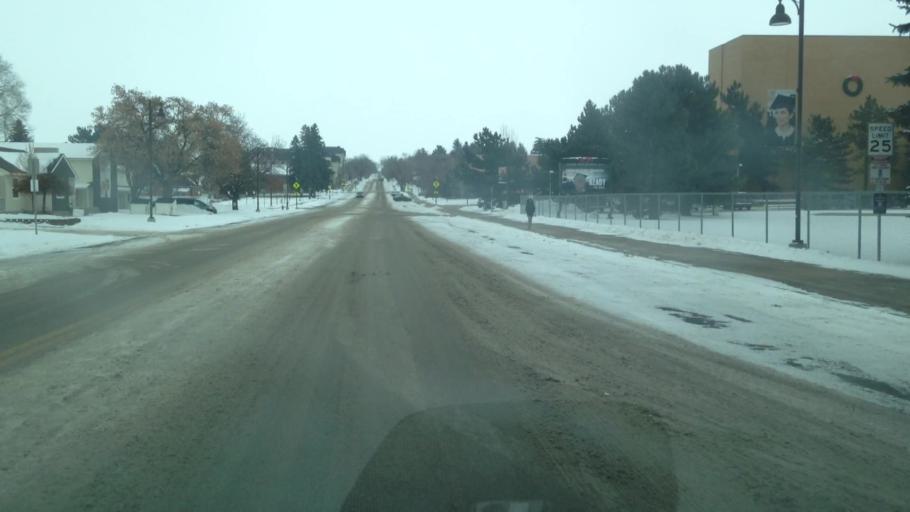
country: US
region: Idaho
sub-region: Madison County
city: Rexburg
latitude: 43.8219
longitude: -111.7858
